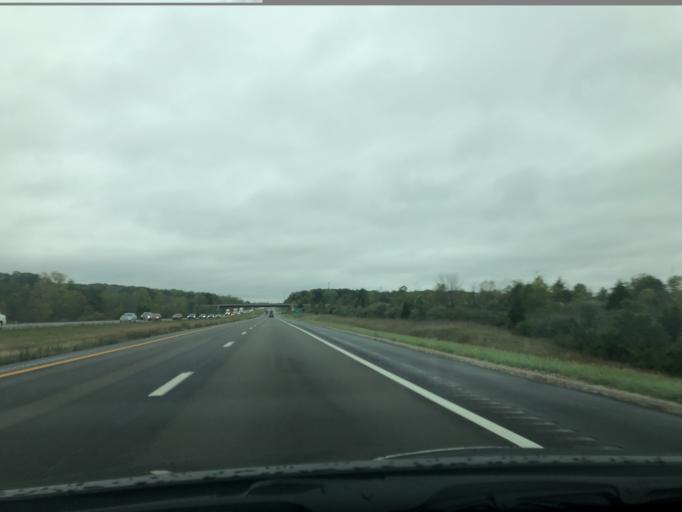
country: US
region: Ohio
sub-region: Champaign County
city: North Lewisburg
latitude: 40.2615
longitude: -83.4722
